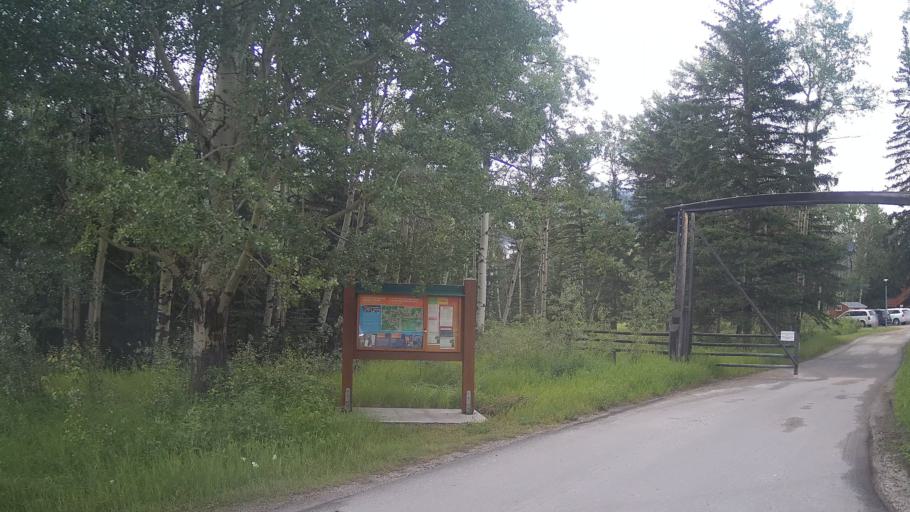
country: CA
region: Alberta
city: Jasper Park Lodge
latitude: 52.9641
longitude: -118.0593
